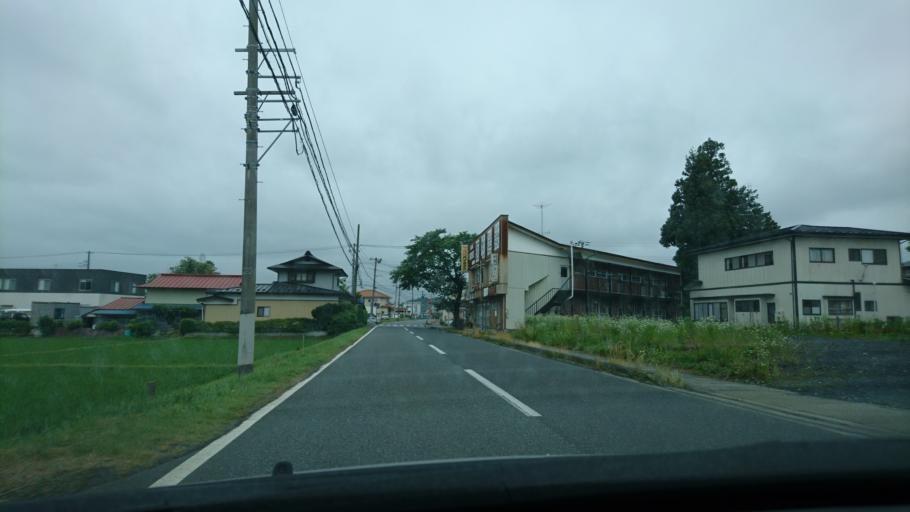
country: JP
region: Iwate
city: Ichinoseki
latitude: 38.9386
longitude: 141.0925
